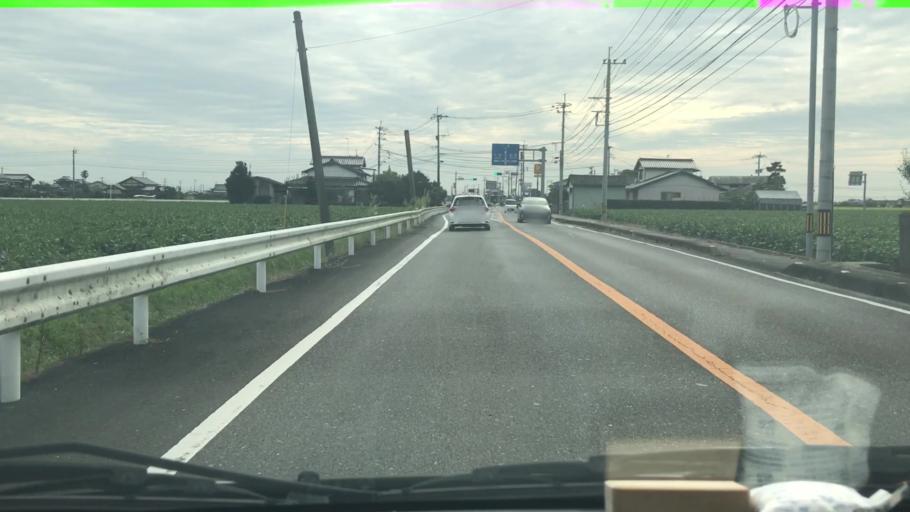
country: JP
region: Saga Prefecture
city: Takeocho-takeo
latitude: 33.1990
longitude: 130.1008
